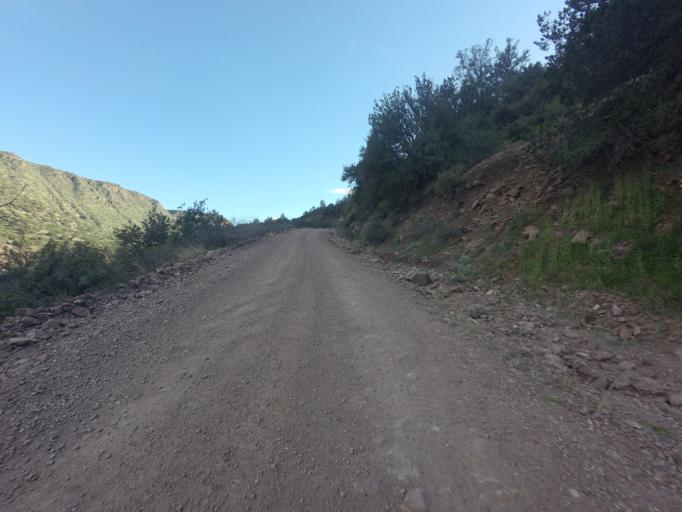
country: US
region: Arizona
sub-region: Gila County
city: Pine
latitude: 34.3804
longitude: -111.6603
